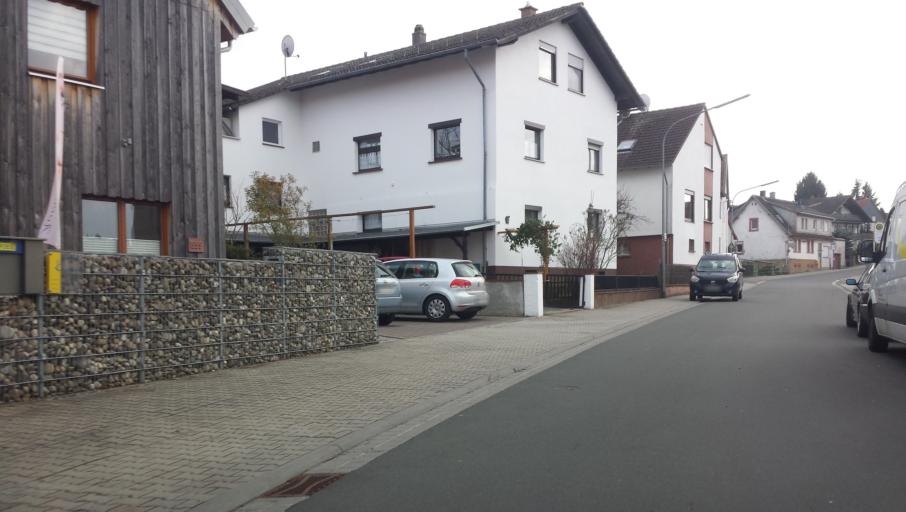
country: DE
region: Hesse
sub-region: Regierungsbezirk Darmstadt
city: Brensbach
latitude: 49.7906
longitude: 8.9349
